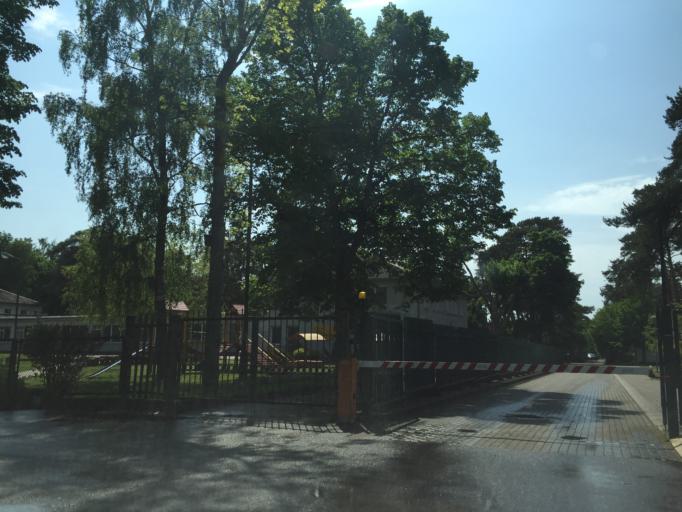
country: LT
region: Klaipedos apskritis
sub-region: Klaipeda
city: Klaipeda
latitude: 55.7685
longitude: 21.0851
